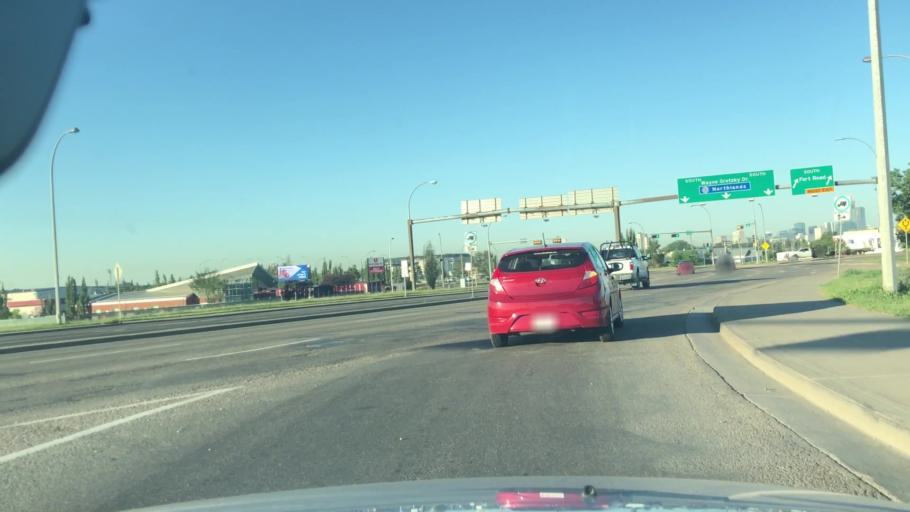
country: CA
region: Alberta
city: Edmonton
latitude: 53.5804
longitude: -113.4536
